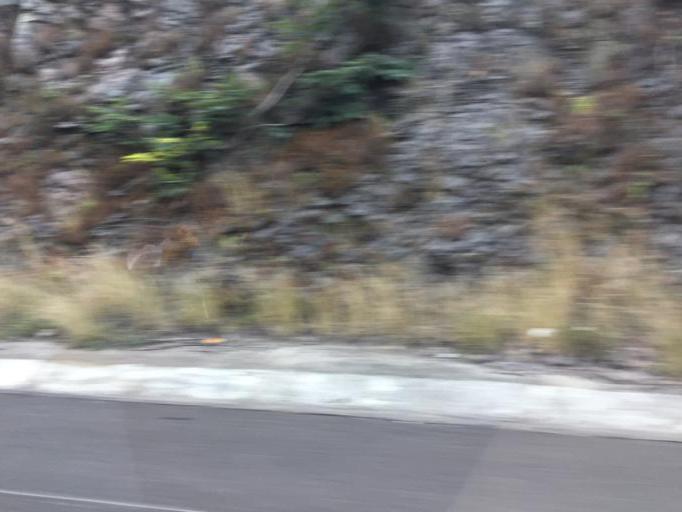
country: MX
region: Michoacan
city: Panindicuaro de la Reforma
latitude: 19.9724
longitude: -101.7246
